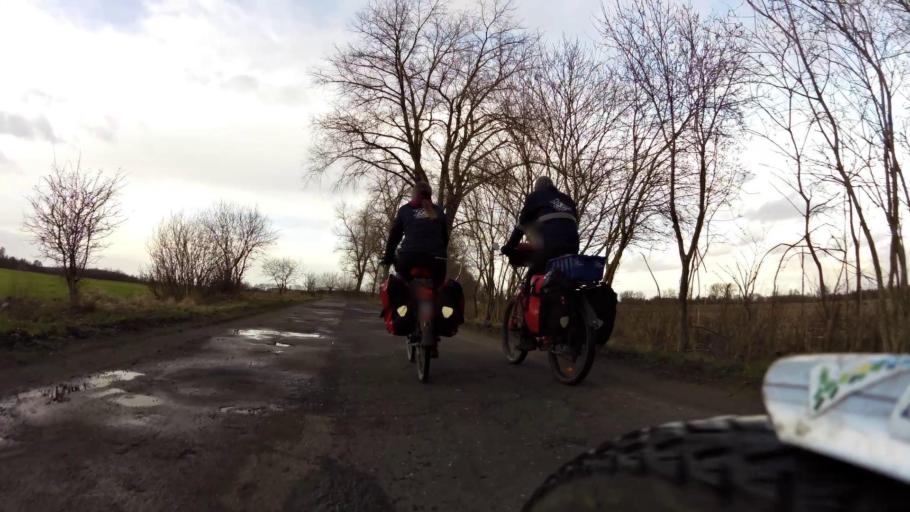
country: PL
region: West Pomeranian Voivodeship
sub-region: Powiat kamienski
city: Kamien Pomorski
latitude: 53.9118
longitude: 14.7309
